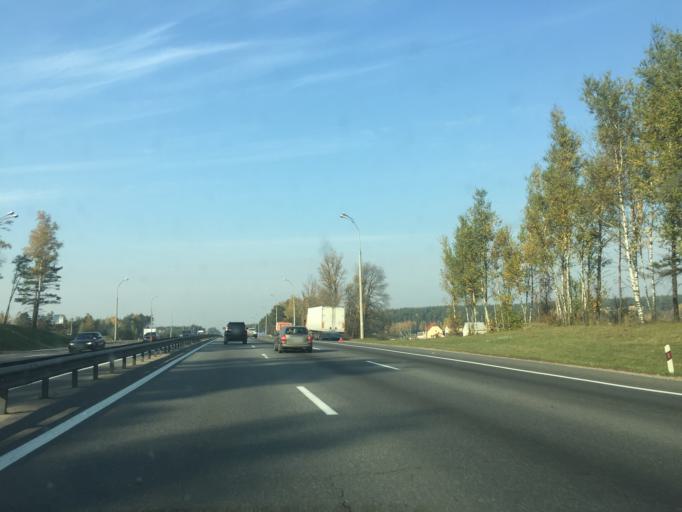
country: BY
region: Minsk
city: Pryvol'ny
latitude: 53.8183
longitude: 27.7670
